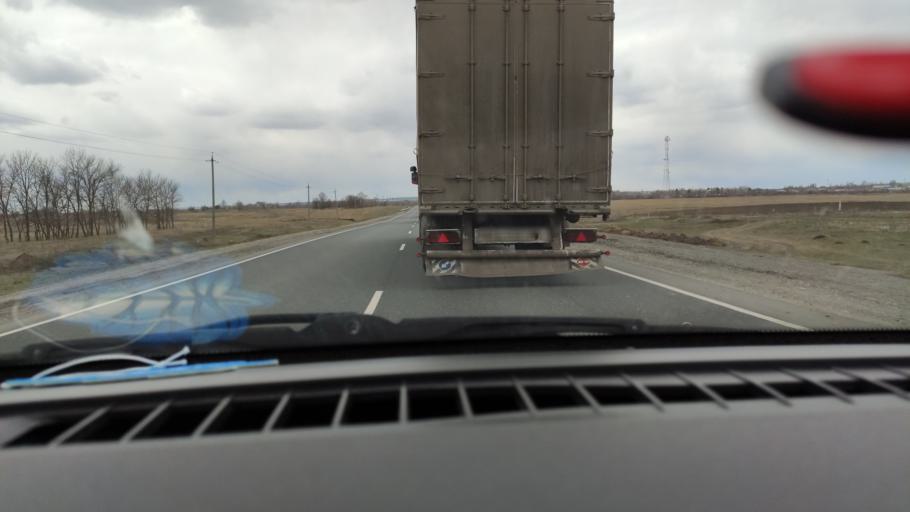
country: RU
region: Saratov
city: Sennoy
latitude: 52.1500
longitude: 46.9811
